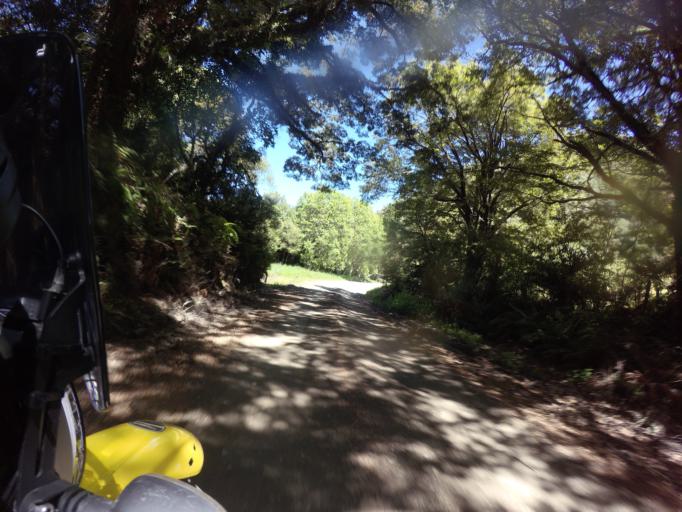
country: NZ
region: Bay of Plenty
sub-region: Opotiki District
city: Opotiki
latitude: -38.4123
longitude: 177.4104
